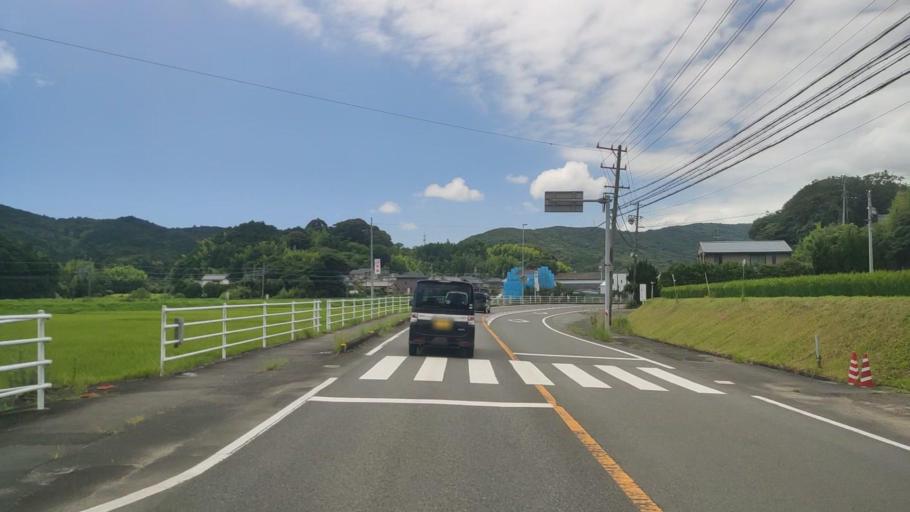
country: JP
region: Mie
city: Toba
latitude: 34.4361
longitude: 136.8413
